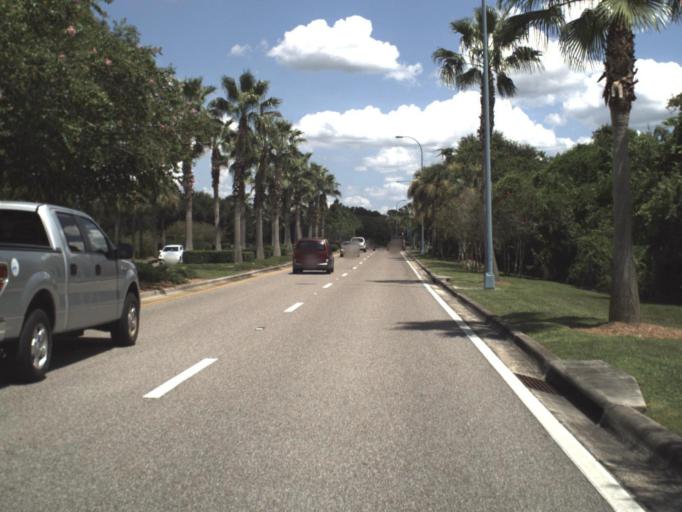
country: US
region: Florida
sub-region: Hillsborough County
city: Brandon
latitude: 27.9283
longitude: -82.3064
